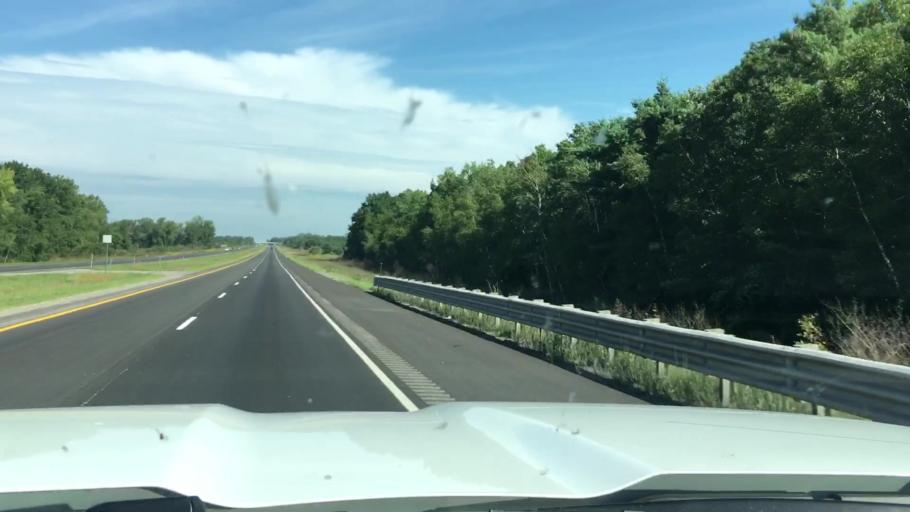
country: US
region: Michigan
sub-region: Saginaw County
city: Freeland
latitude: 43.5475
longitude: -84.1387
